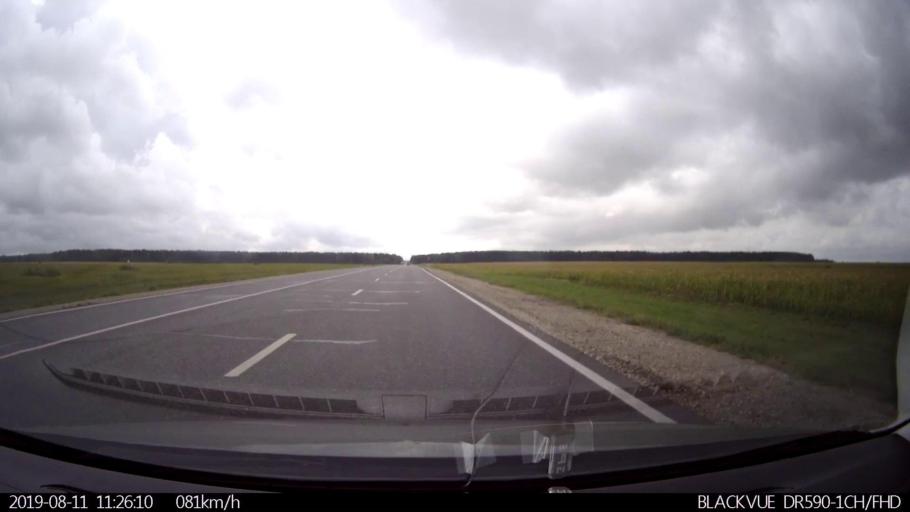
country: RU
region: Ulyanovsk
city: Krasnyy Gulyay
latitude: 54.1088
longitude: 48.2361
